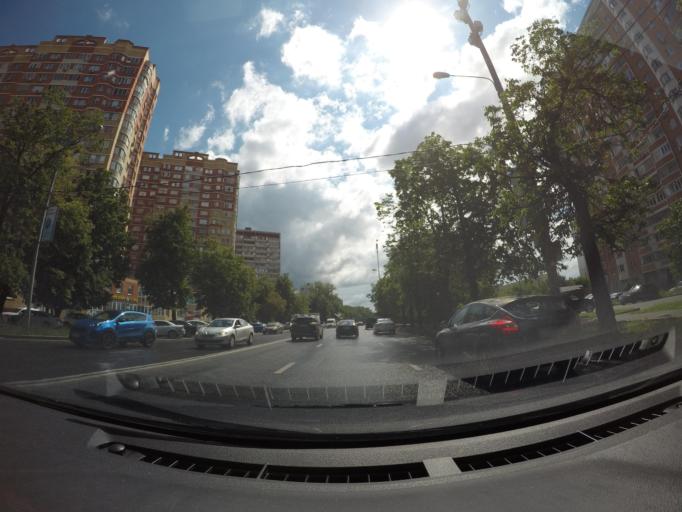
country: RU
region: Moscow
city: Zhulebino
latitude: 55.6979
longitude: 37.8580
